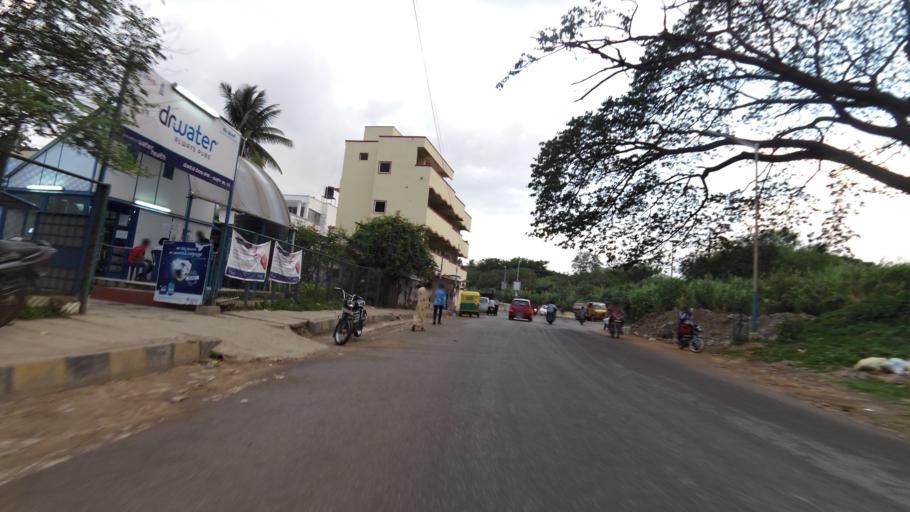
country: IN
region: Karnataka
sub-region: Bangalore Urban
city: Bangalore
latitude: 13.0021
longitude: 77.6387
